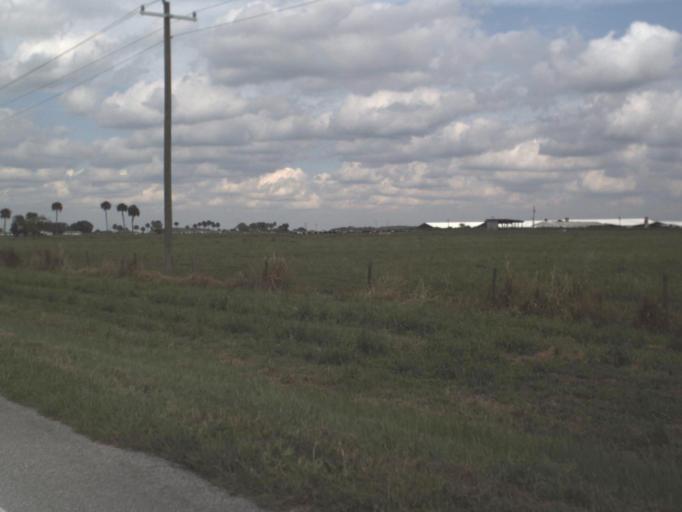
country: US
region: Florida
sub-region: Okeechobee County
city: Cypress Quarters
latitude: 27.4085
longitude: -80.8143
